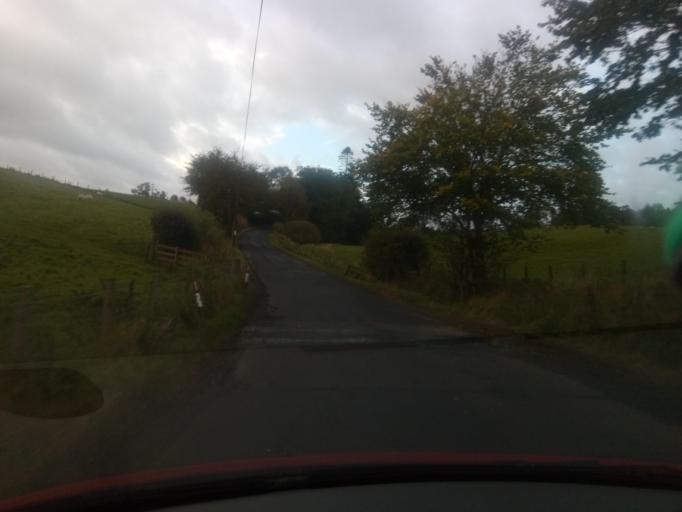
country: GB
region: Scotland
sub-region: The Scottish Borders
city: Jedburgh
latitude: 55.4515
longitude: -2.5677
